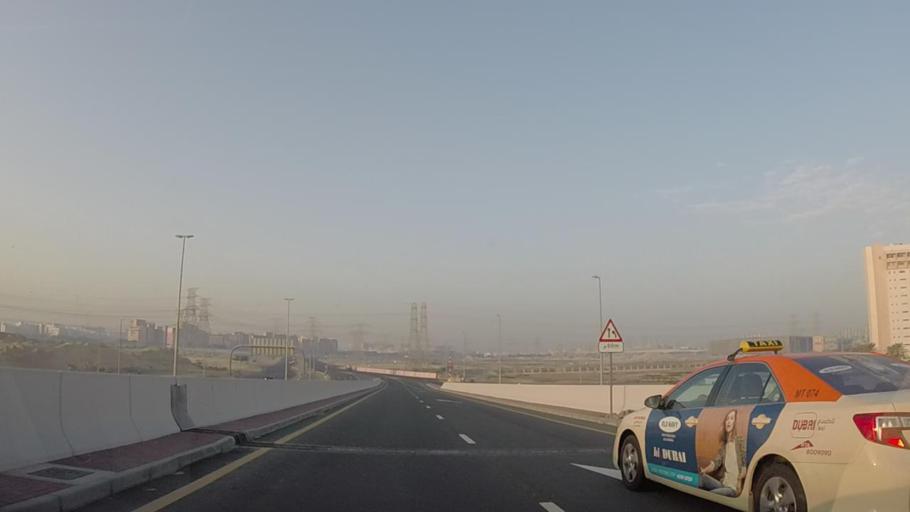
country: AE
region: Dubai
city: Dubai
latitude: 25.0571
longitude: 55.1381
